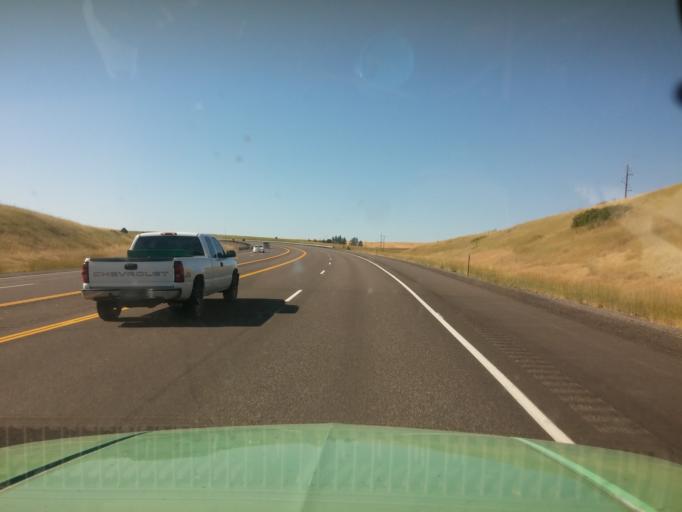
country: US
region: Washington
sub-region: Asotin County
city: Clarkston
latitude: 46.4794
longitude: -117.0384
